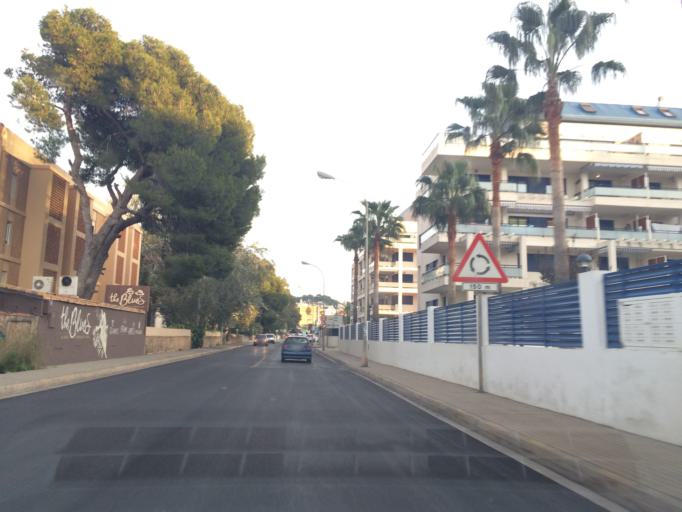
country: ES
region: Valencia
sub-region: Provincia de Alicante
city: Denia
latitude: 38.8360
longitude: 0.1185
